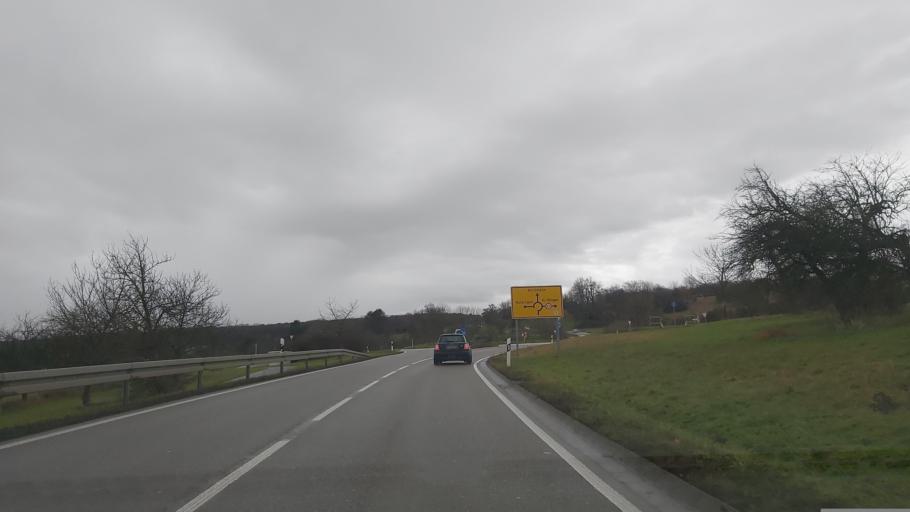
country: DE
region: Baden-Wuerttemberg
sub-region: Regierungsbezirk Stuttgart
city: Notzingen
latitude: 48.6678
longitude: 9.4338
